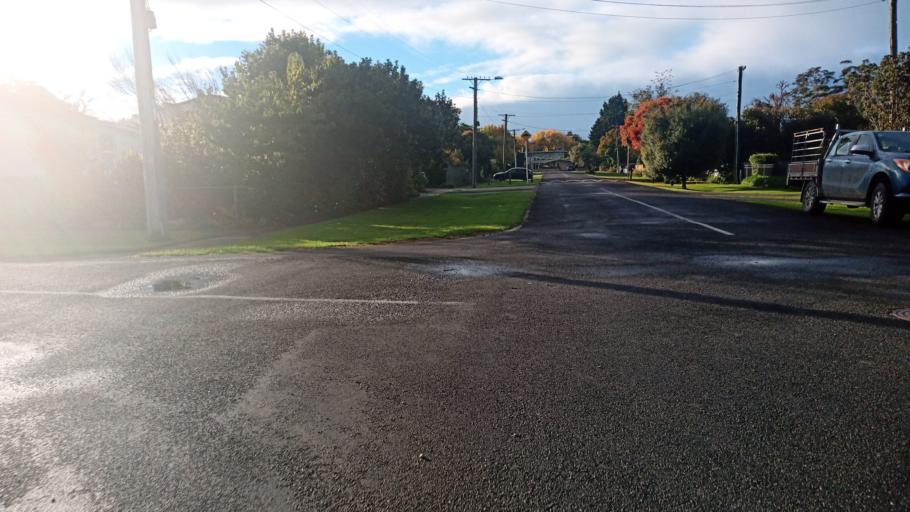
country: NZ
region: Gisborne
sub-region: Gisborne District
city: Gisborne
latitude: -38.6521
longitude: 178.0177
